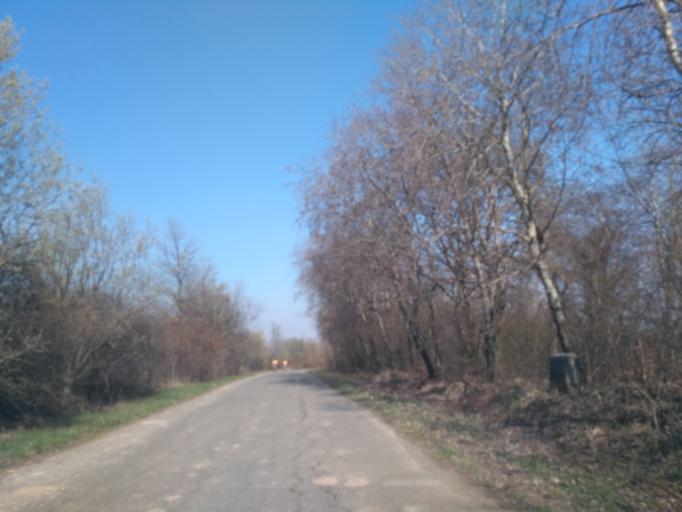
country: SK
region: Presovsky
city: Vranov nad Topl'ou
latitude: 48.8117
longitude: 21.6377
